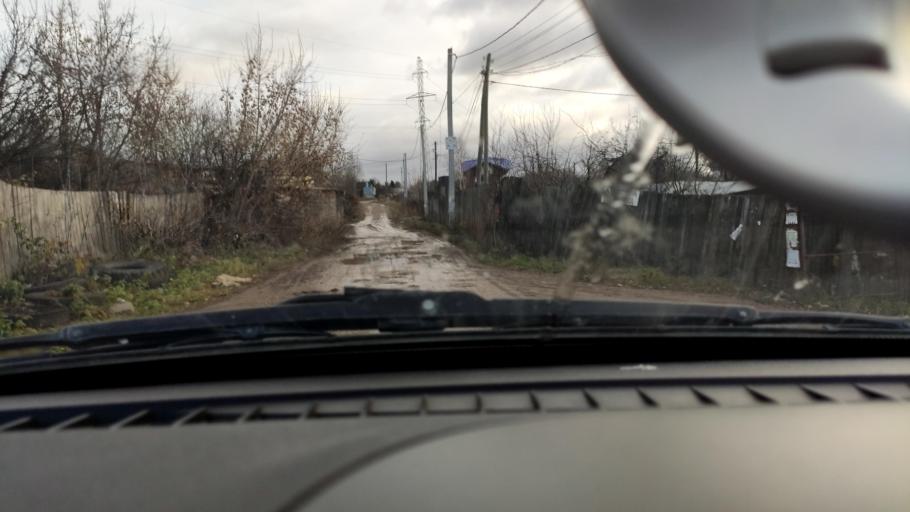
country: RU
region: Perm
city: Kondratovo
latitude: 57.9567
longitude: 56.1458
